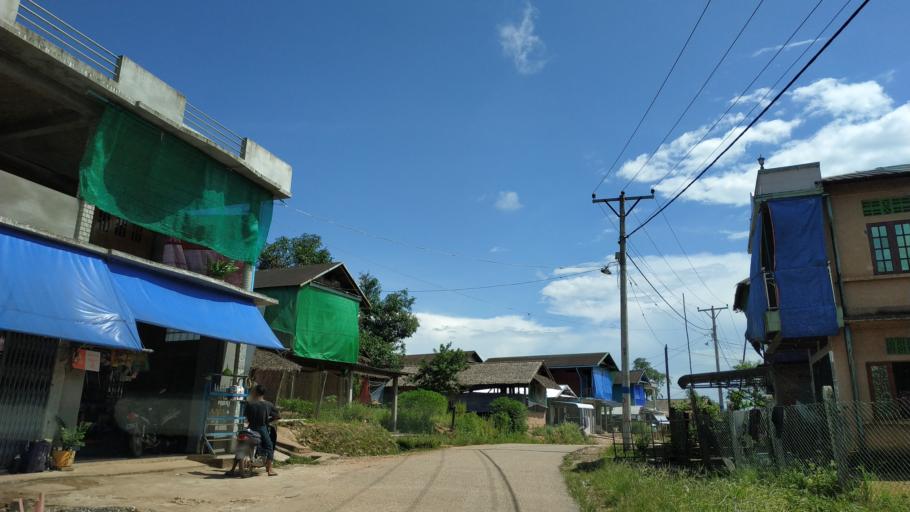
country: MM
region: Tanintharyi
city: Dawei
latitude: 14.2140
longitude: 98.1925
